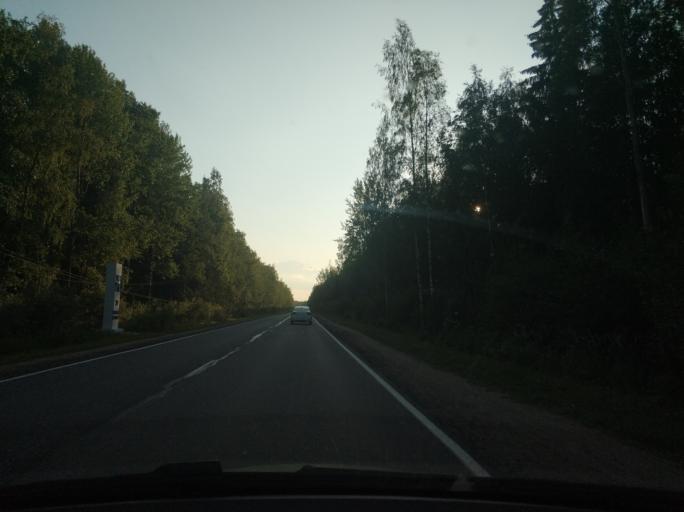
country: RU
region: Leningrad
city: Borisova Griva
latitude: 60.0817
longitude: 31.0540
